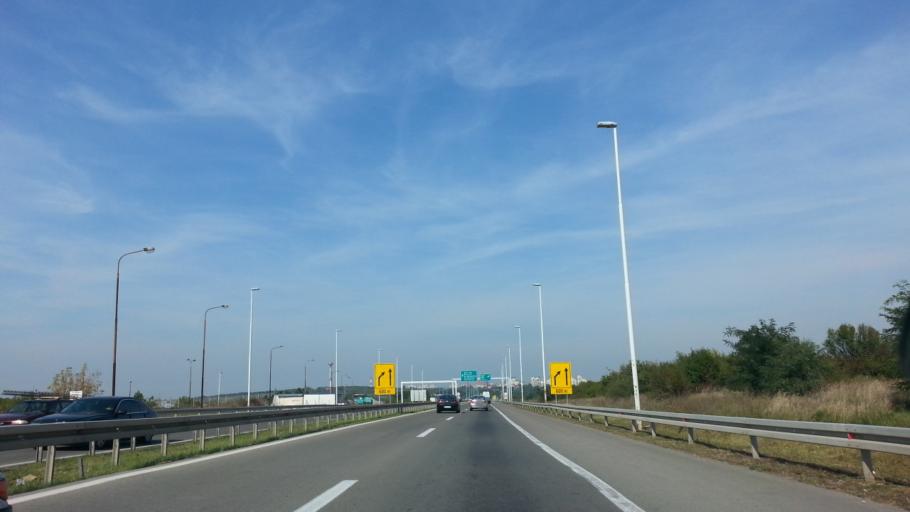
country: RS
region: Central Serbia
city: Sremcica
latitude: 44.7051
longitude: 20.4133
